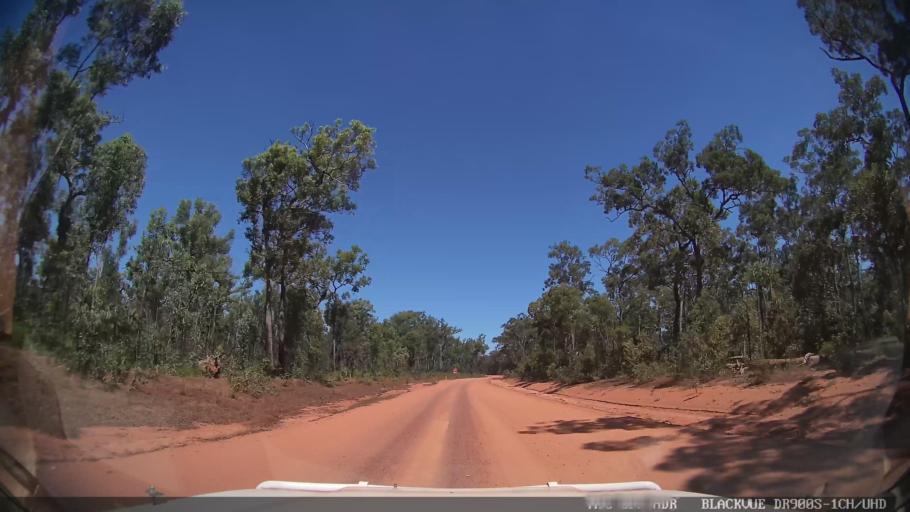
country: AU
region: Queensland
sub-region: Torres
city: Thursday Island
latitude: -11.1845
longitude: 142.2544
